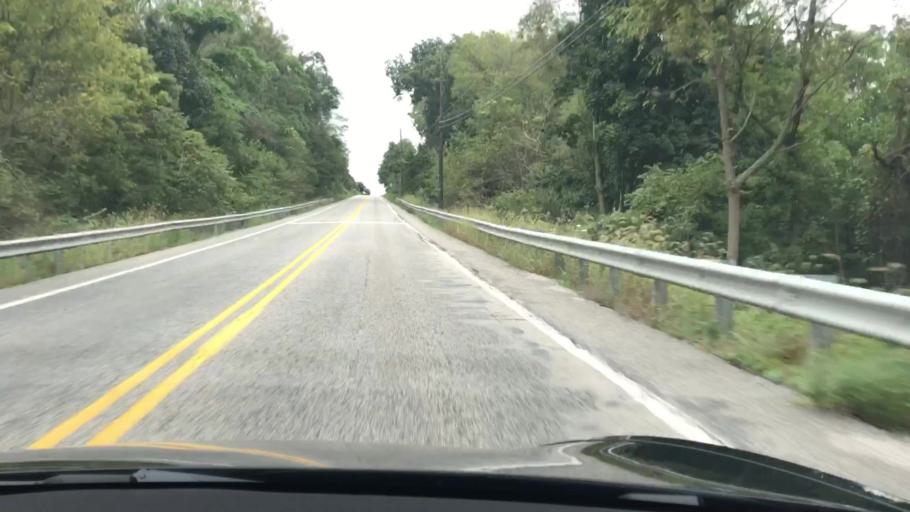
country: US
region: Pennsylvania
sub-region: Cumberland County
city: Mechanicsburg
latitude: 40.1587
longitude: -76.9715
